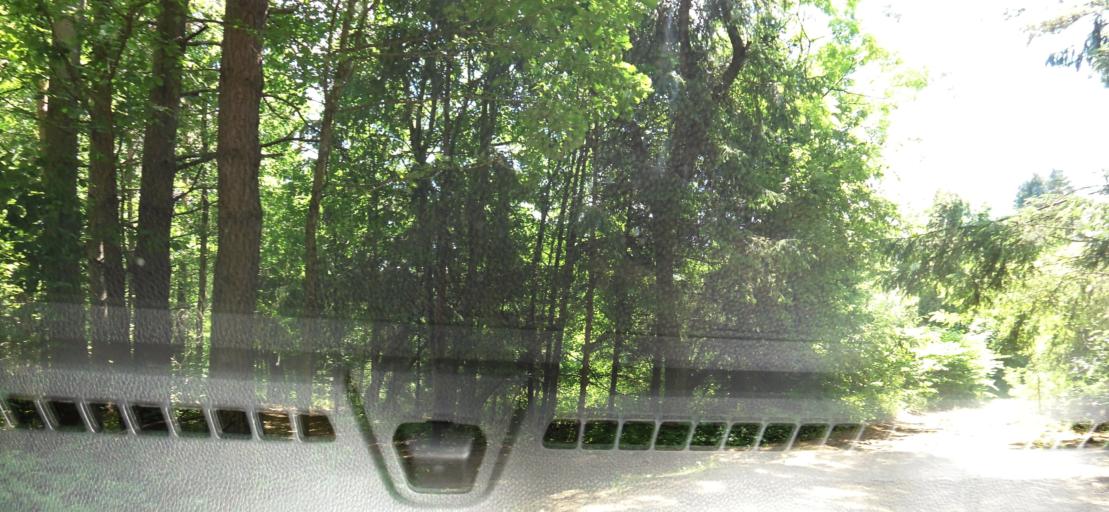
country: LT
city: Nemencine
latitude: 54.8744
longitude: 25.5758
